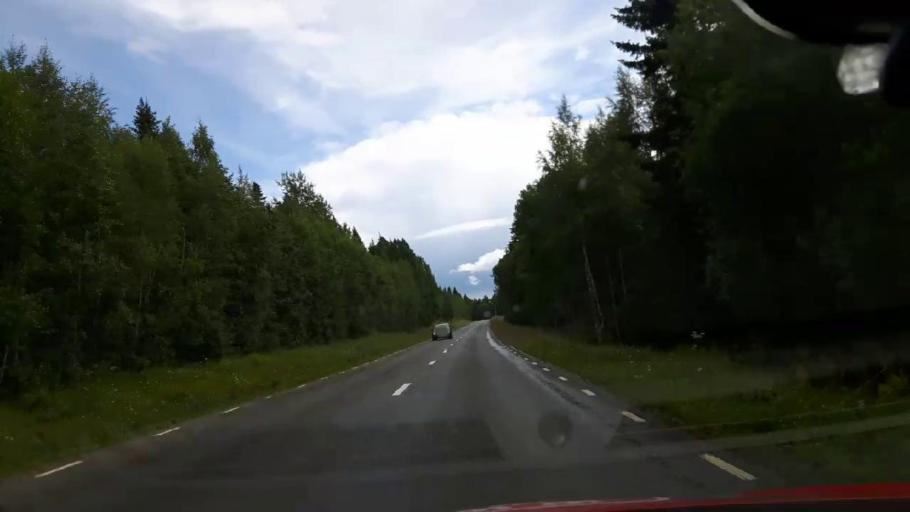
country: SE
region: Jaemtland
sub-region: Stroemsunds Kommun
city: Stroemsund
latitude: 64.3406
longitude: 14.9500
